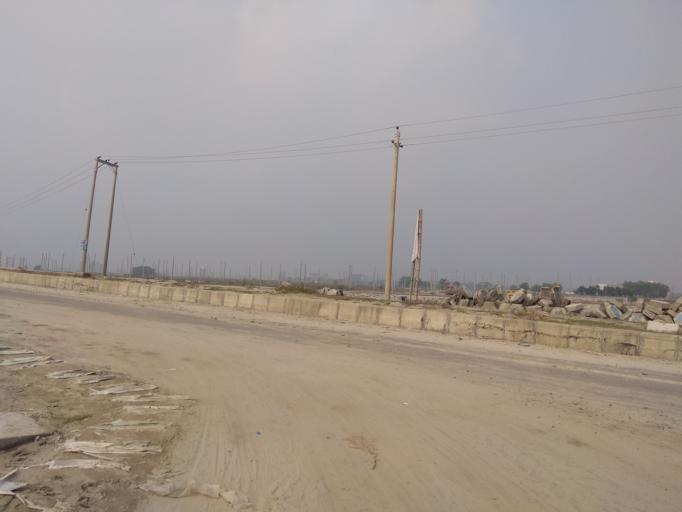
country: BD
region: Dhaka
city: Tungi
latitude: 23.8598
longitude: 90.3728
